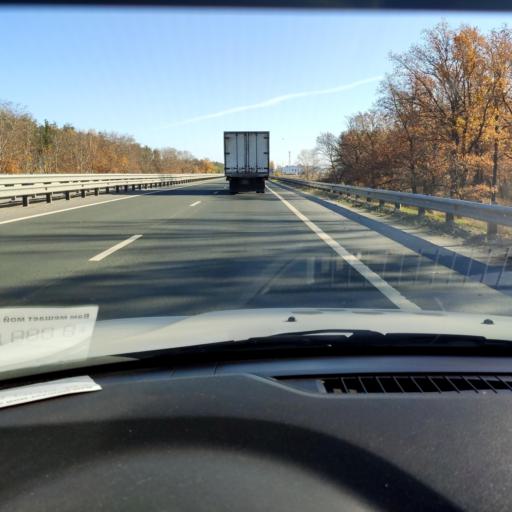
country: RU
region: Samara
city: Zhigulevsk
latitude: 53.5130
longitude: 49.5834
